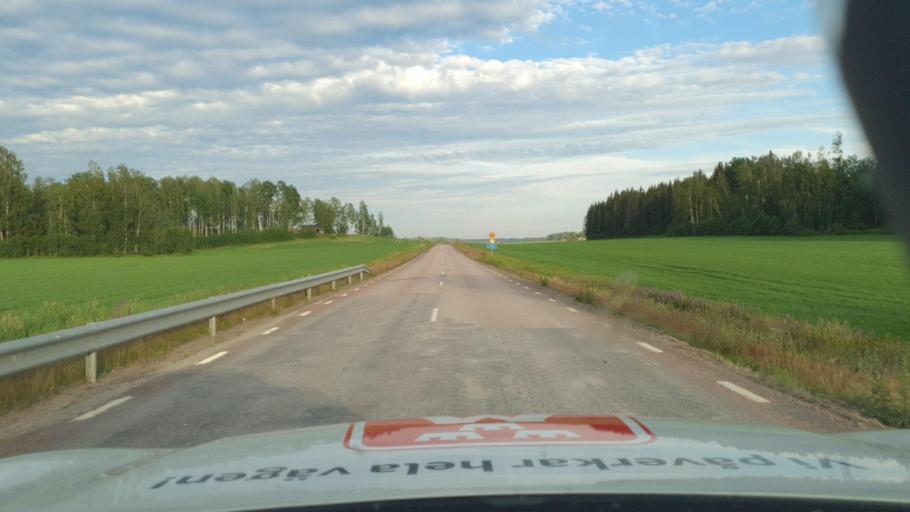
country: SE
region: Vaermland
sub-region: Karlstads Kommun
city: Molkom
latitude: 59.4680
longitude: 13.8126
